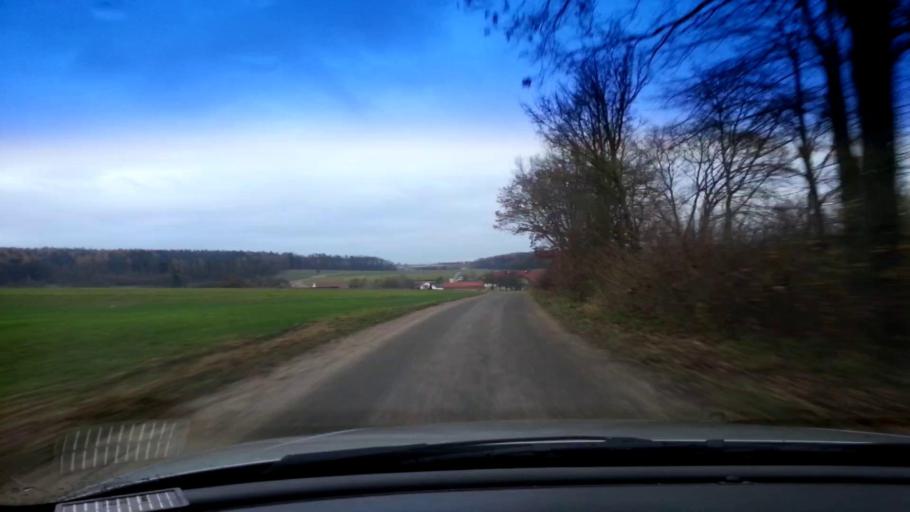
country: DE
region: Bavaria
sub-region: Upper Franconia
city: Litzendorf
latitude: 49.9418
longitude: 11.0116
